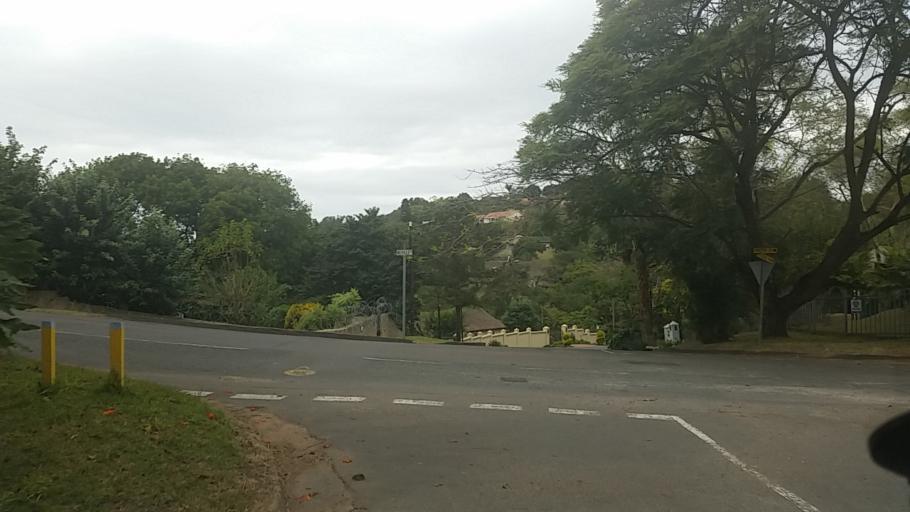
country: ZA
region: KwaZulu-Natal
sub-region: eThekwini Metropolitan Municipality
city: Berea
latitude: -29.8388
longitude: 30.9315
